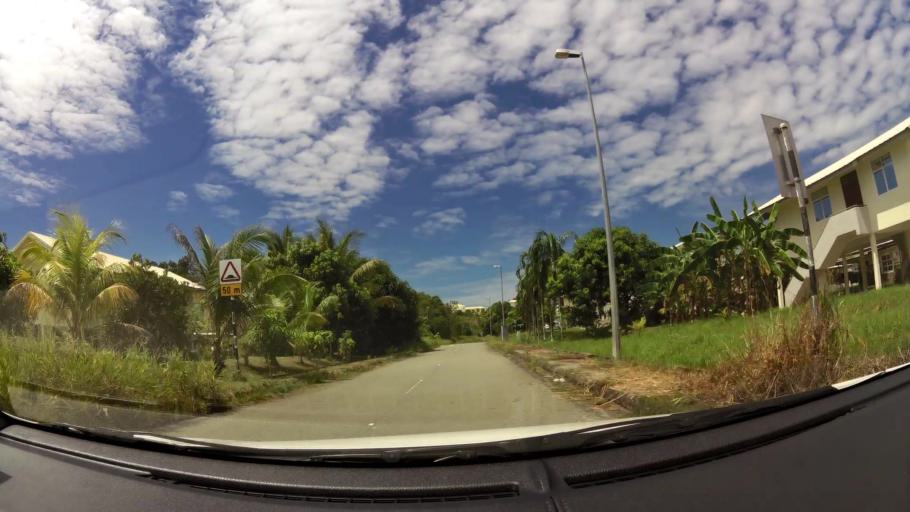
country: BN
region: Brunei and Muara
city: Bandar Seri Begawan
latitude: 4.9930
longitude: 115.0093
